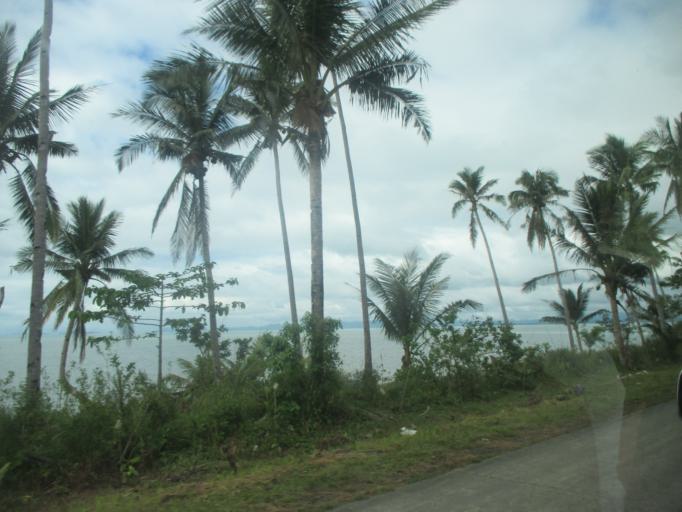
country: PH
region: Eastern Visayas
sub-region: Province of Samar
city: Basey
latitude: 11.2461
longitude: 125.1721
